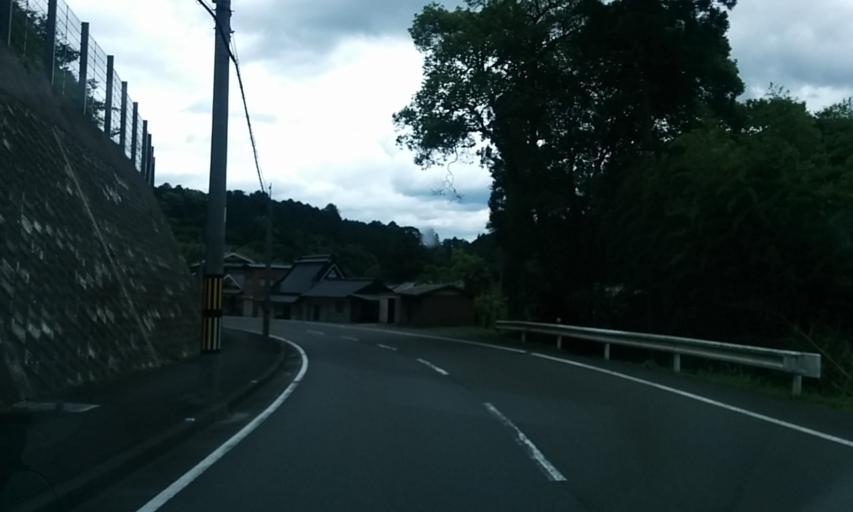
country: JP
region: Kyoto
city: Kameoka
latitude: 35.0929
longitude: 135.4244
